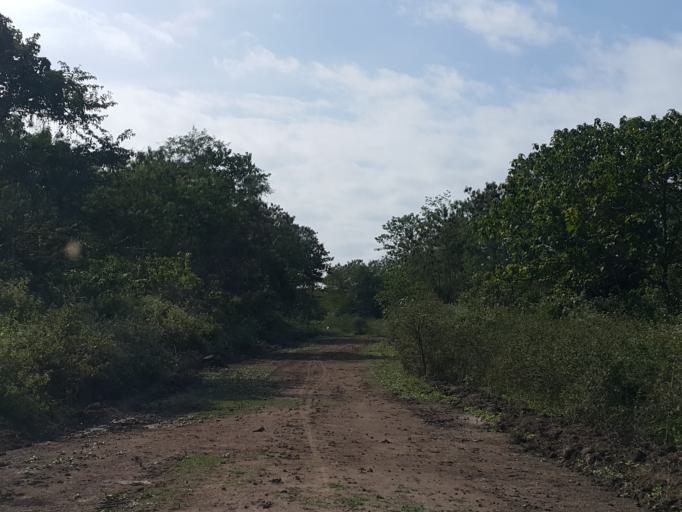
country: TH
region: Lampang
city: Mae Mo
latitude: 18.3397
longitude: 99.7659
